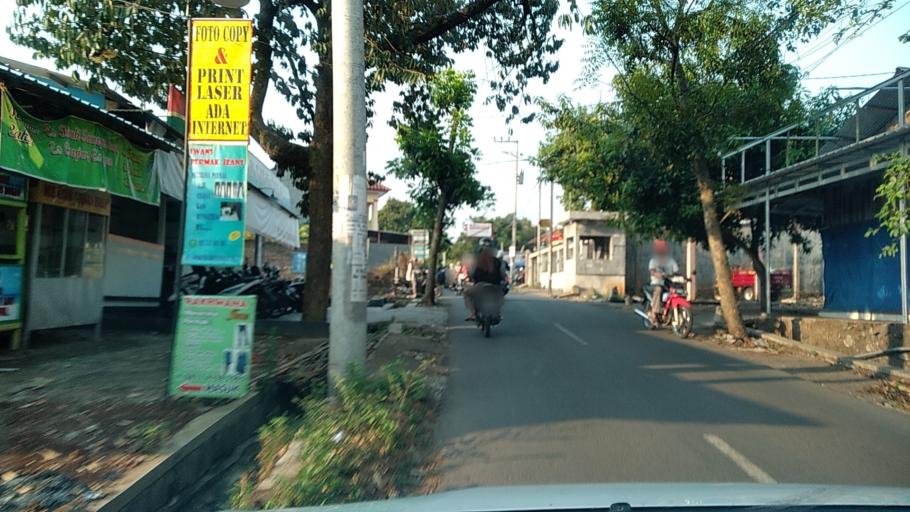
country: ID
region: Central Java
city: Semarang
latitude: -7.0656
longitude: 110.4405
